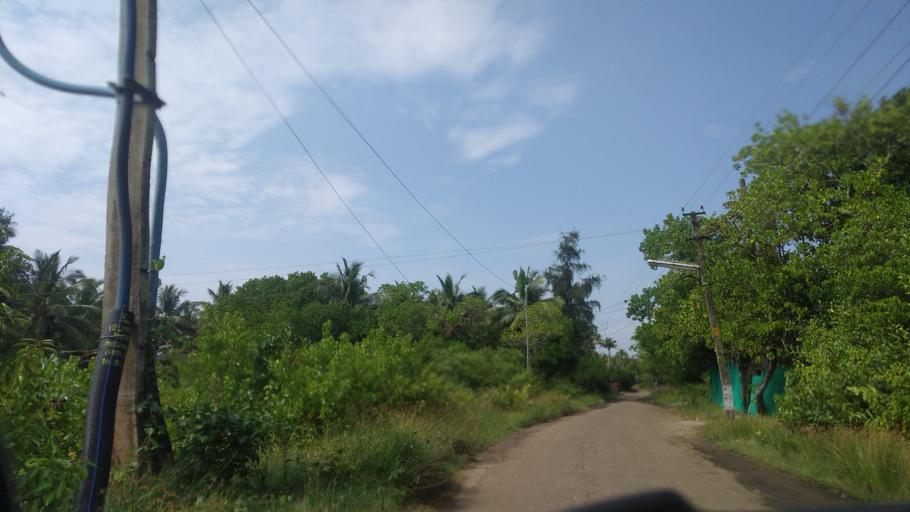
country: IN
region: Kerala
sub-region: Ernakulam
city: Elur
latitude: 10.0528
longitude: 76.2031
